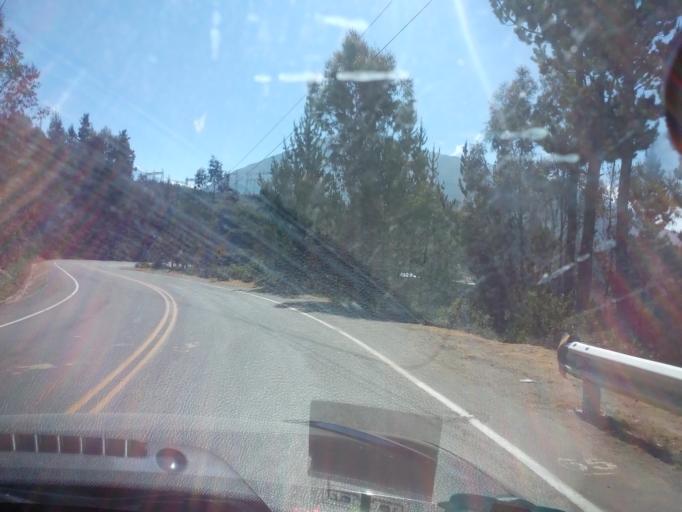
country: PE
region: Apurimac
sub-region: Provincia de Abancay
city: Cachora
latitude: -13.5416
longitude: -72.8031
